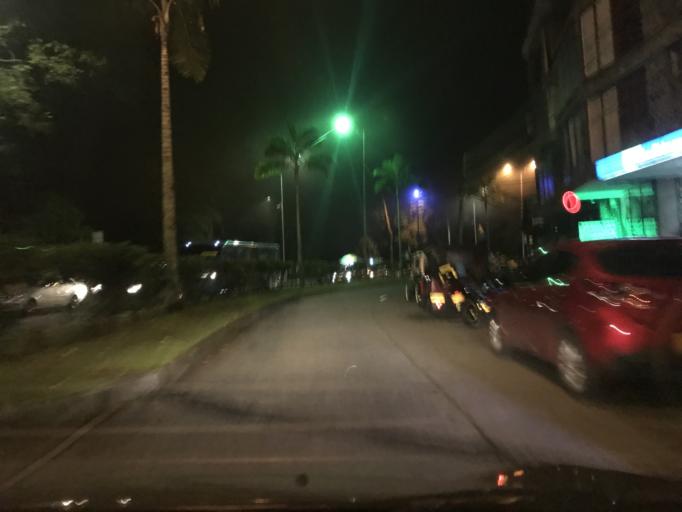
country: CO
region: Caldas
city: Manizales
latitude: 5.0751
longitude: -75.5282
